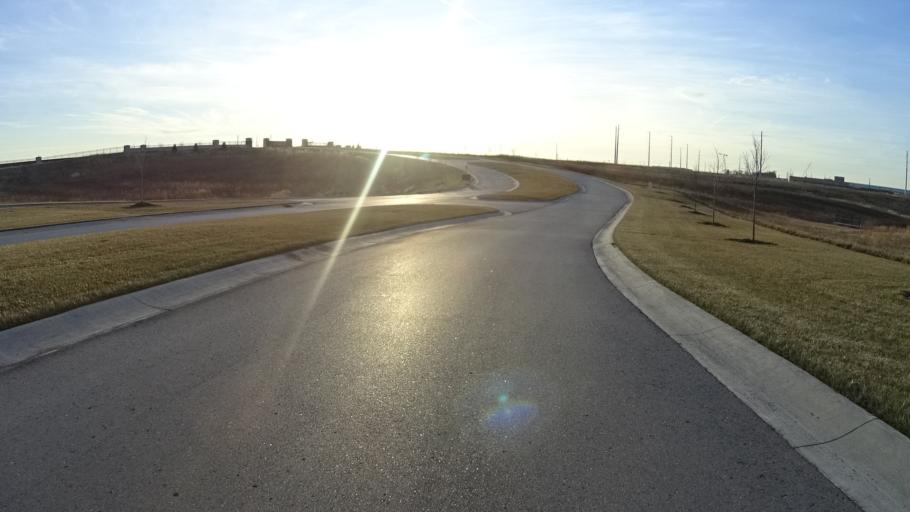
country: US
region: Nebraska
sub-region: Sarpy County
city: Springfield
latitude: 41.1342
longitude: -96.1335
